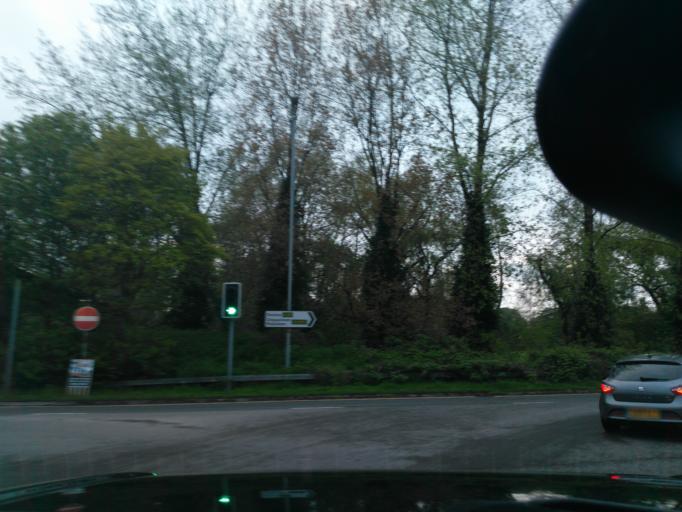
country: GB
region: England
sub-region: Wiltshire
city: Trowbridge
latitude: 51.3172
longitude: -2.2037
